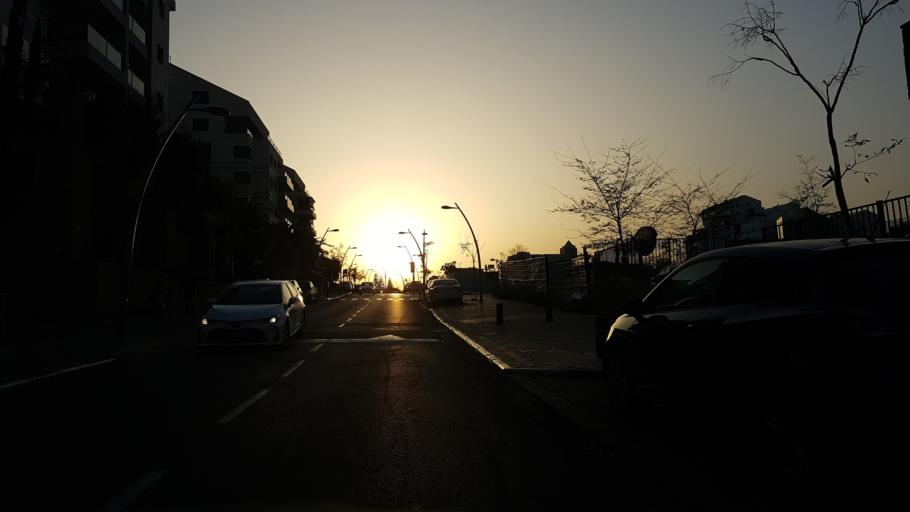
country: IL
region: Central District
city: Ra'anana
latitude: 32.1945
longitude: 34.8919
